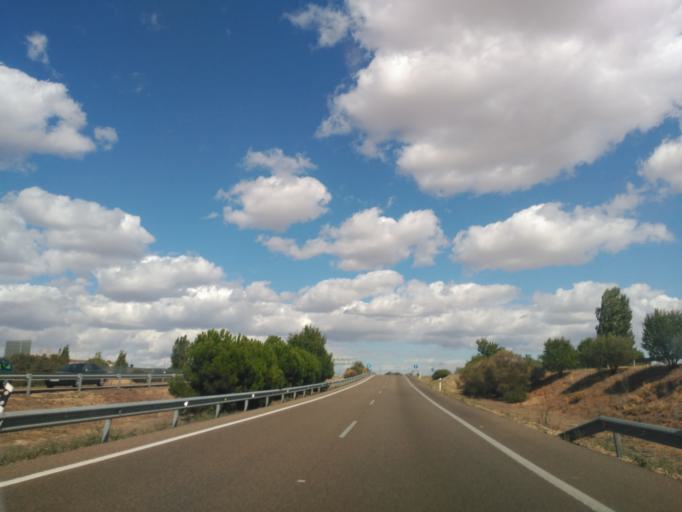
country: ES
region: Castille and Leon
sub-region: Provincia de Palencia
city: Reinoso de Cerrato
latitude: 42.0045
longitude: -4.3678
